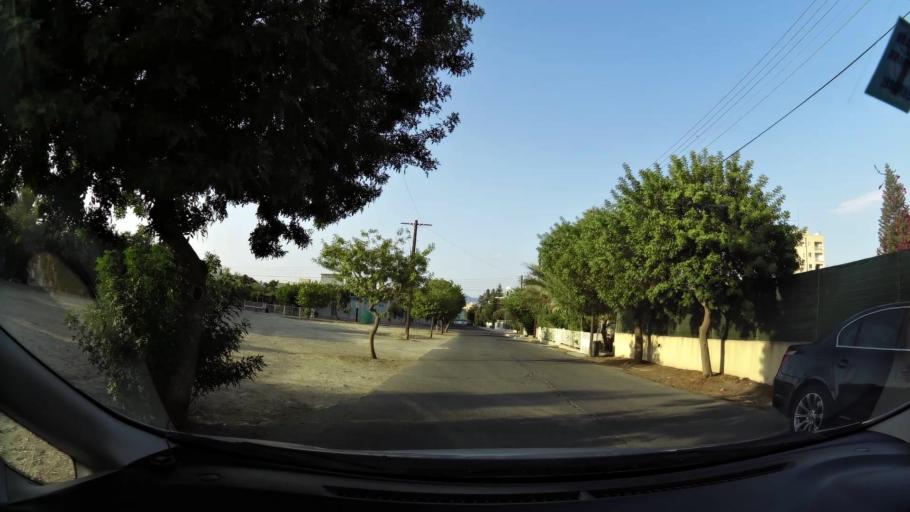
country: CY
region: Lefkosia
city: Nicosia
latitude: 35.1723
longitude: 33.3422
